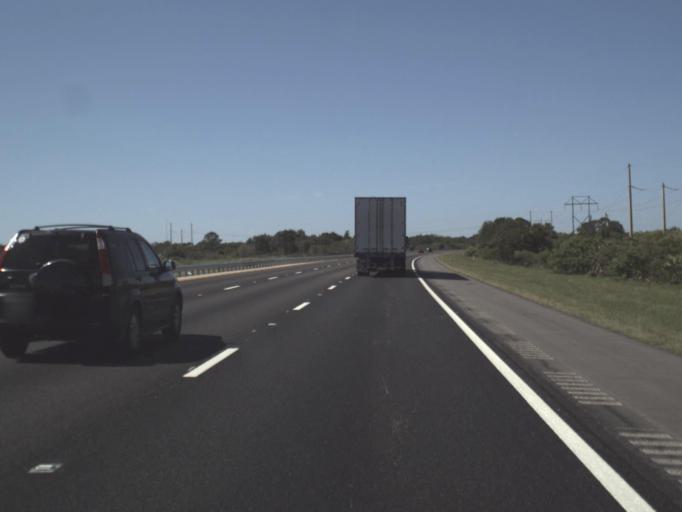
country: US
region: Florida
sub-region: Lee County
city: Suncoast Estates
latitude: 26.7249
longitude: -81.8305
